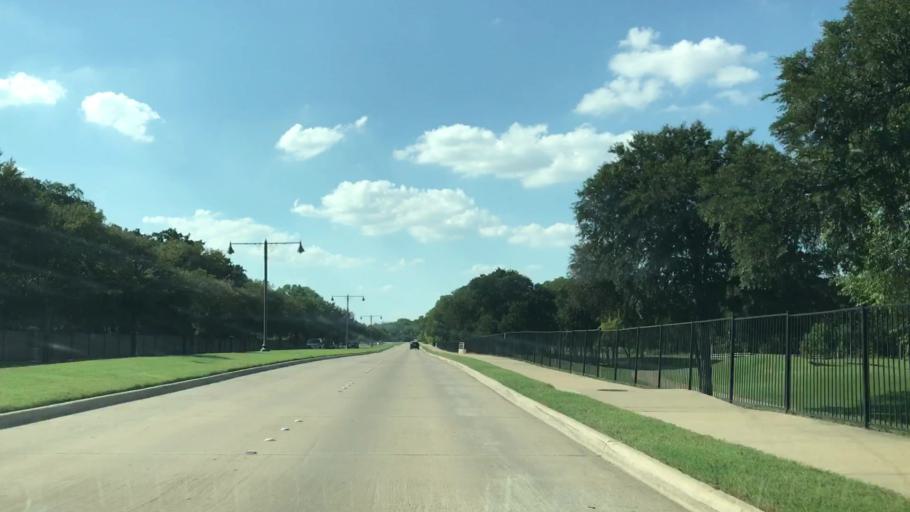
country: US
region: Texas
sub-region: Tarrant County
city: Keller
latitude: 32.9235
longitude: -97.2151
